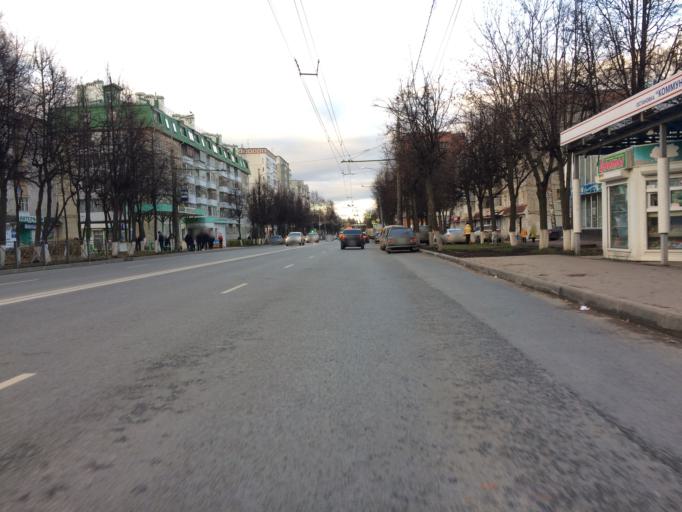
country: RU
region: Mariy-El
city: Yoshkar-Ola
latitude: 56.6405
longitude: 47.8889
